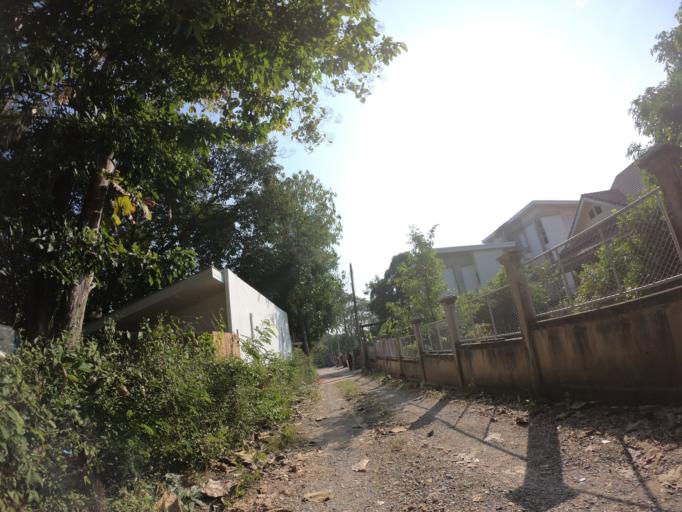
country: TH
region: Chiang Mai
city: Chiang Mai
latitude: 18.7865
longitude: 98.9533
